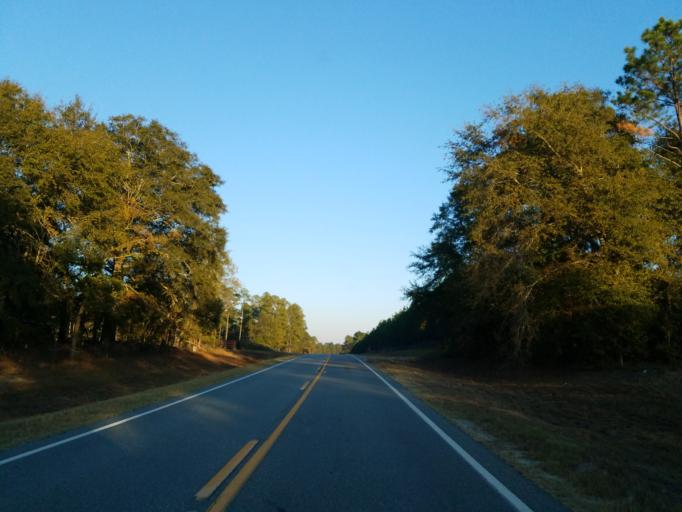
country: US
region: Georgia
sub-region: Turner County
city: Ashburn
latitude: 31.8239
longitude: -83.5567
